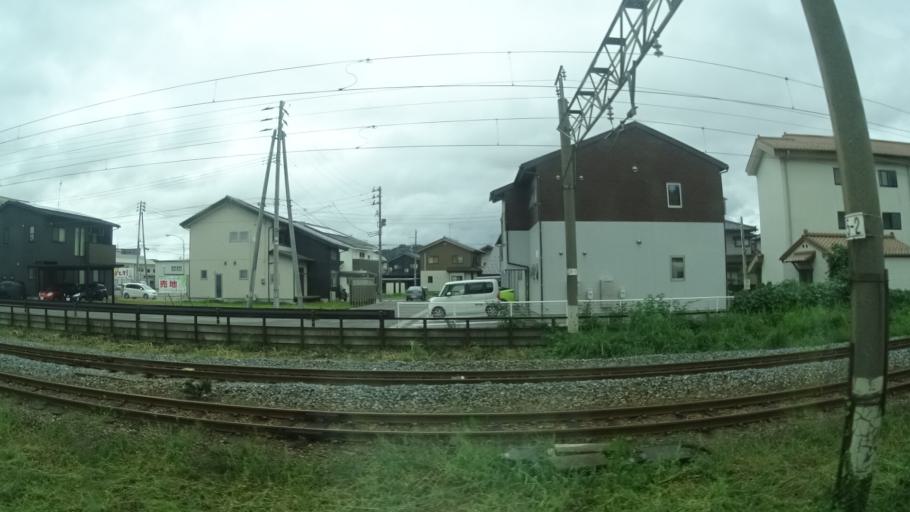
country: JP
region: Niigata
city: Murakami
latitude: 38.2181
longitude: 139.4633
